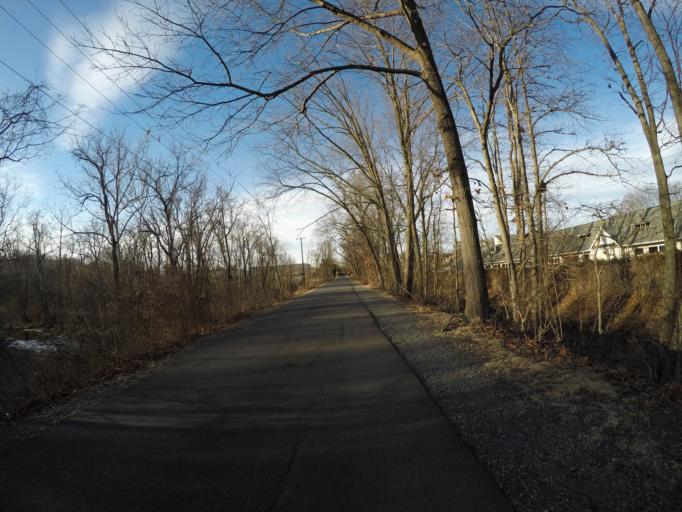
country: US
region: Virginia
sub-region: Loudoun County
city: Leesburg
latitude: 39.0989
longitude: -77.5456
